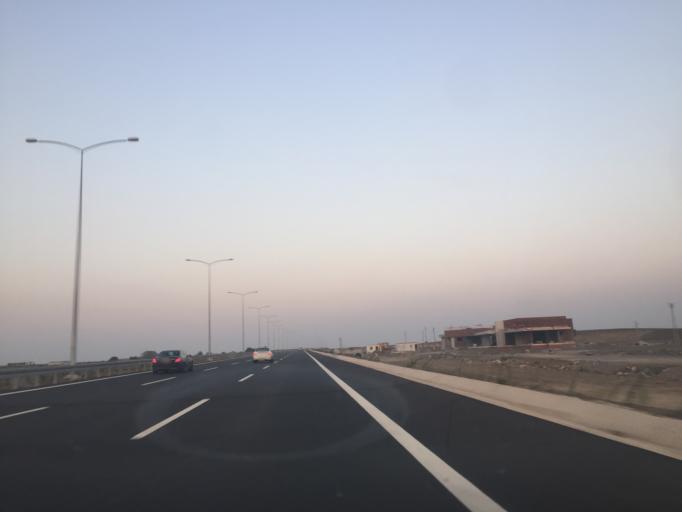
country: TR
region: Bursa
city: Mahmudiye
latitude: 40.2729
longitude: 28.5989
